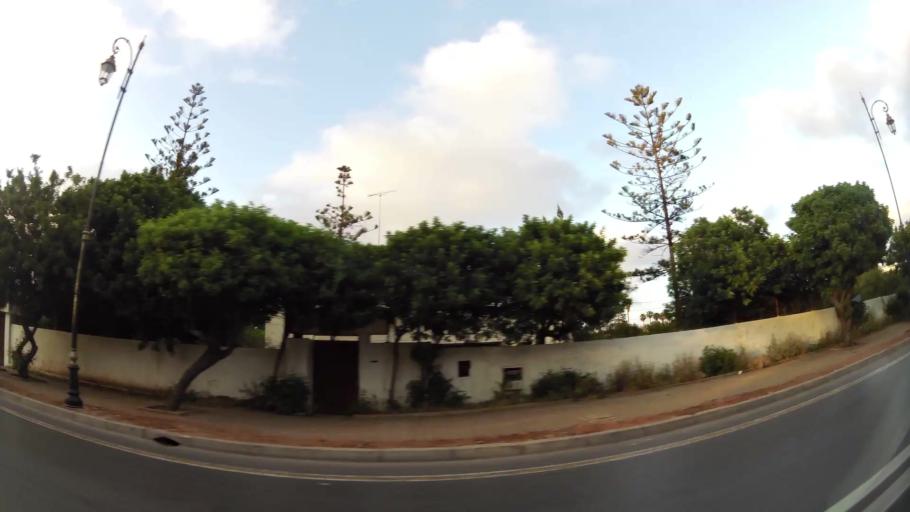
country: MA
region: Rabat-Sale-Zemmour-Zaer
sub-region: Rabat
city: Rabat
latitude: 33.9761
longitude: -6.8375
